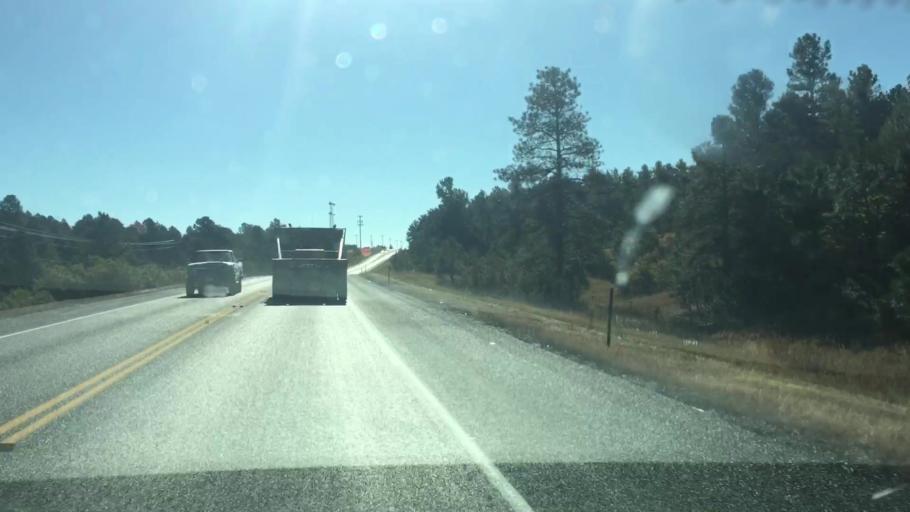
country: US
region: Colorado
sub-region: Elbert County
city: Ponderosa Park
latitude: 39.3737
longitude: -104.6869
